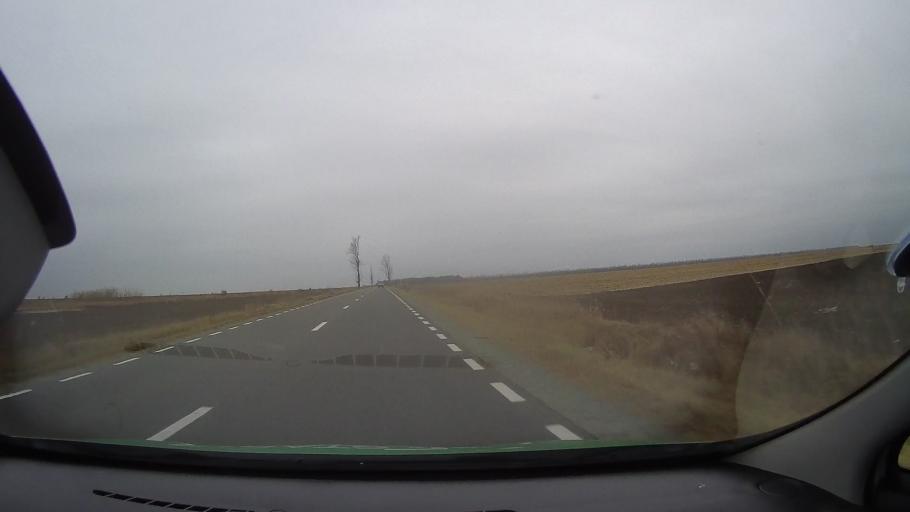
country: RO
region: Ialomita
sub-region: Comuna Scanteia
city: Iazu
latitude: 44.7127
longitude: 27.4192
